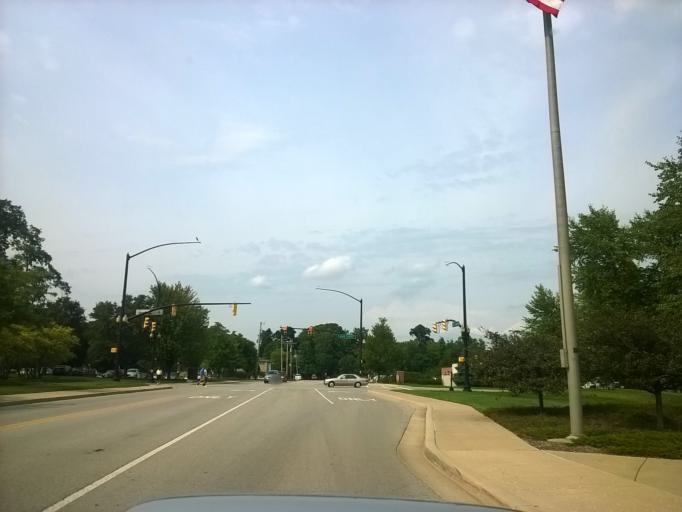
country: US
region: Indiana
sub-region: Hamilton County
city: Carmel
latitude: 39.9779
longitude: -86.1226
